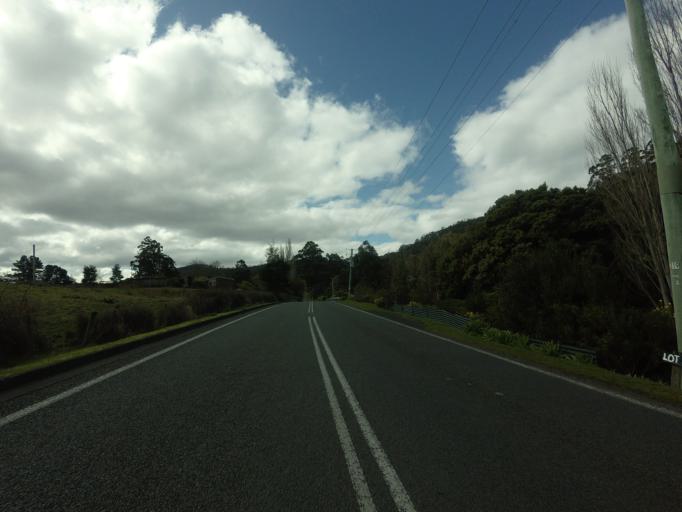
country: AU
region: Tasmania
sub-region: Huon Valley
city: Geeveston
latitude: -43.2995
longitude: 147.0085
